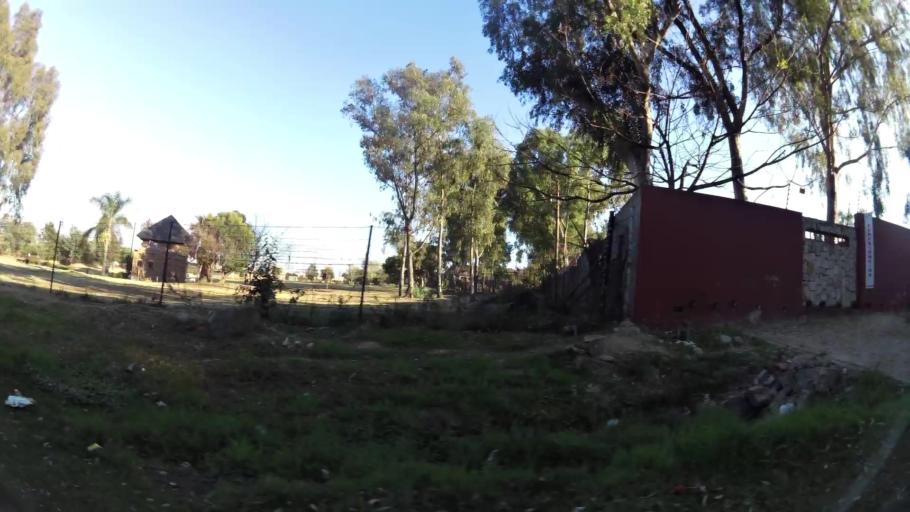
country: ZA
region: Gauteng
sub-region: City of Johannesburg Metropolitan Municipality
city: Midrand
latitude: -26.0233
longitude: 28.1313
